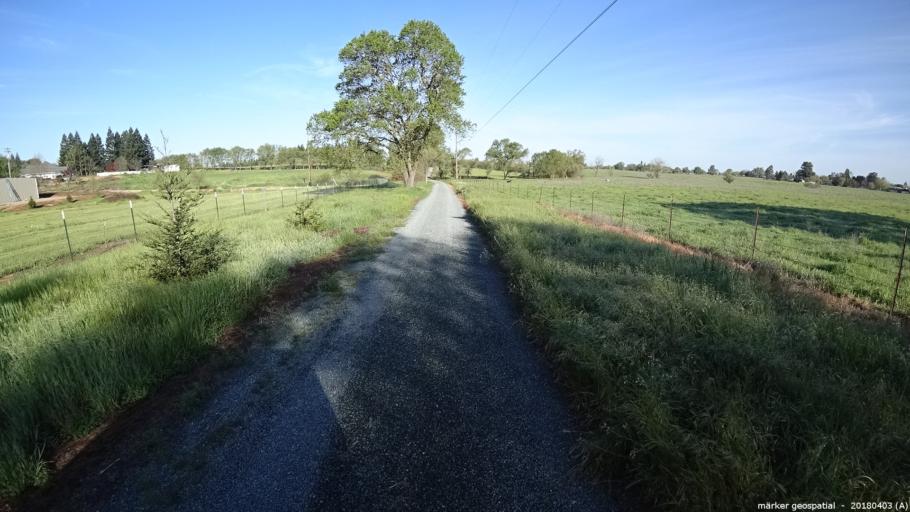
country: US
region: California
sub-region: Sacramento County
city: Wilton
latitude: 38.4389
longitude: -121.1998
